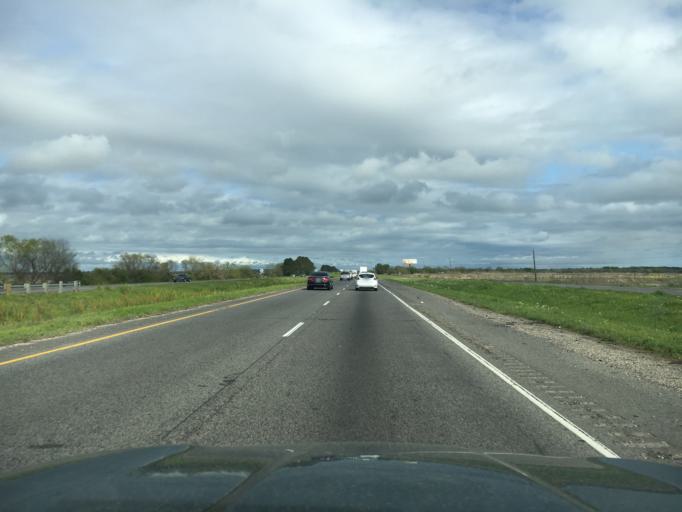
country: US
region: Louisiana
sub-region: Jefferson Davis Parish
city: Jennings
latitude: 30.2463
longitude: -92.7074
